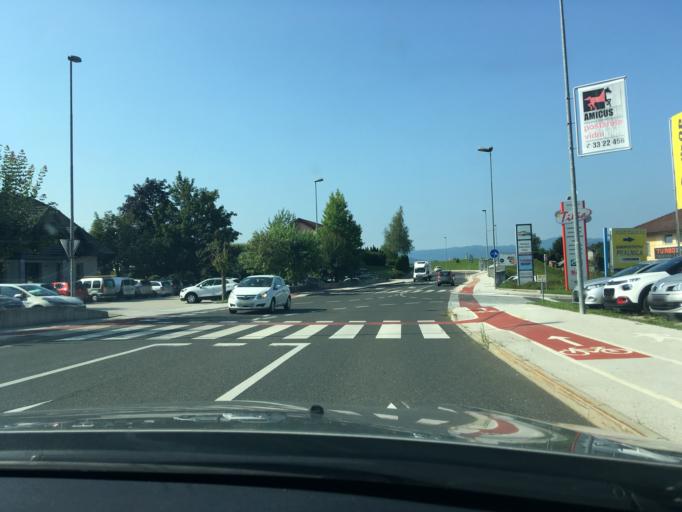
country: SI
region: Novo Mesto
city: Novo Mesto
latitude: 45.8286
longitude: 15.1570
